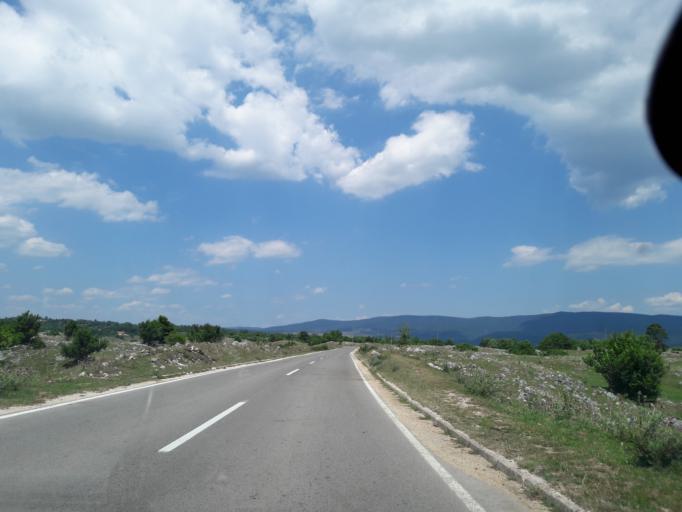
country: BA
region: Republika Srpska
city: Sipovo
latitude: 44.1589
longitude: 17.1697
